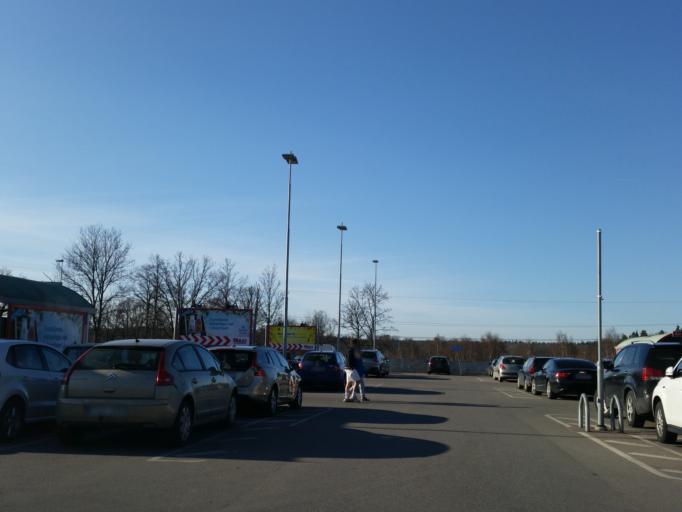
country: SE
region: Kalmar
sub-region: Oskarshamns Kommun
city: Oskarshamn
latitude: 57.2659
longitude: 16.4337
